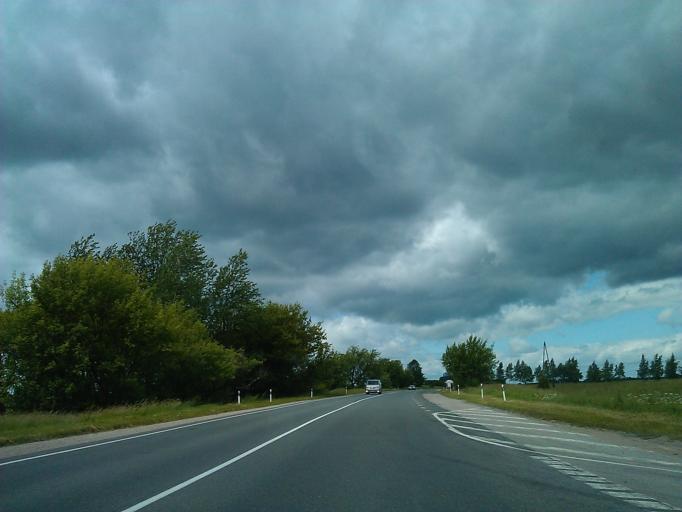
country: LV
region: Engure
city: Smarde
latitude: 56.9198
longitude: 23.2626
